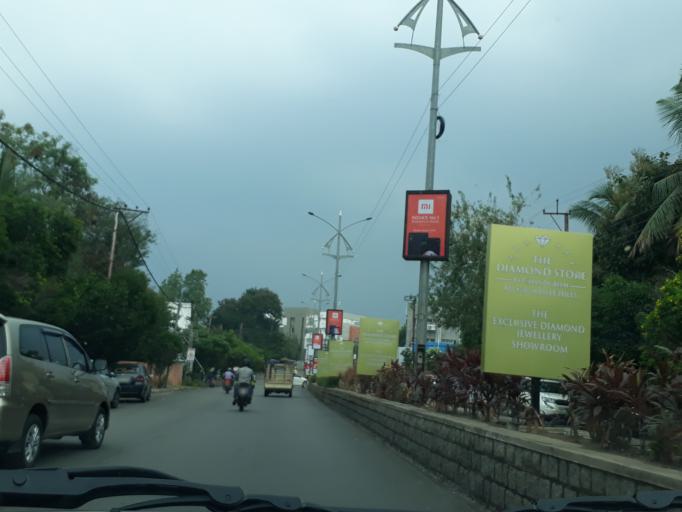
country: IN
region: Telangana
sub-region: Rangareddi
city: Kukatpalli
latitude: 17.4346
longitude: 78.4147
